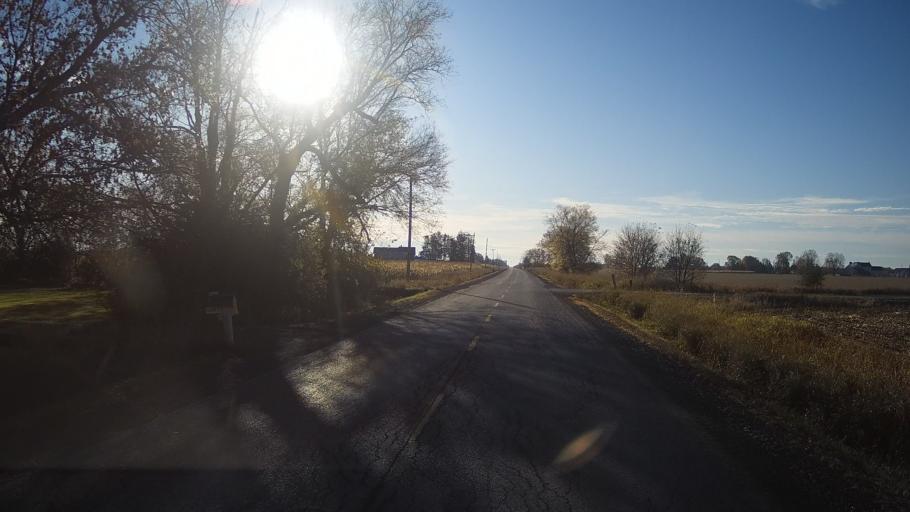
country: CA
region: Ontario
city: Arnprior
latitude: 45.3634
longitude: -76.2477
